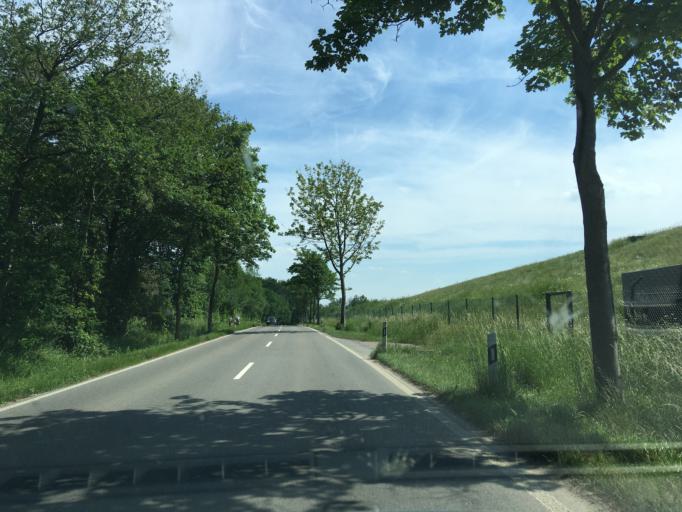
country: DE
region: North Rhine-Westphalia
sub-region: Regierungsbezirk Munster
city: Borken
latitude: 51.8367
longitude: 6.7814
